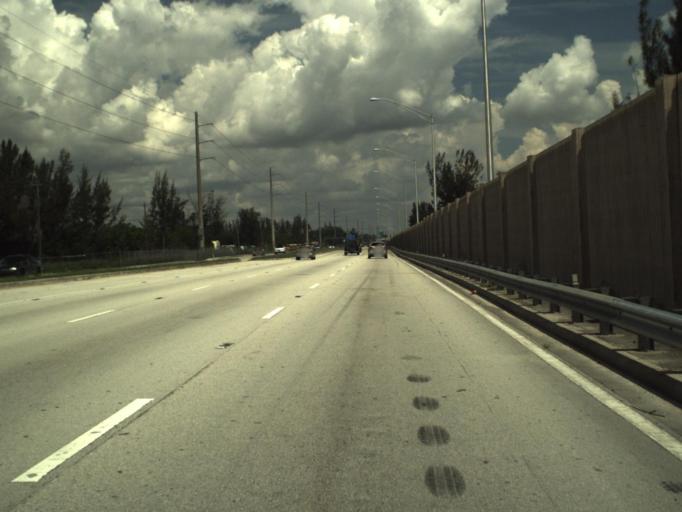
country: US
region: Florida
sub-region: Miami-Dade County
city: Tamiami
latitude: 25.7672
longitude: -80.4171
